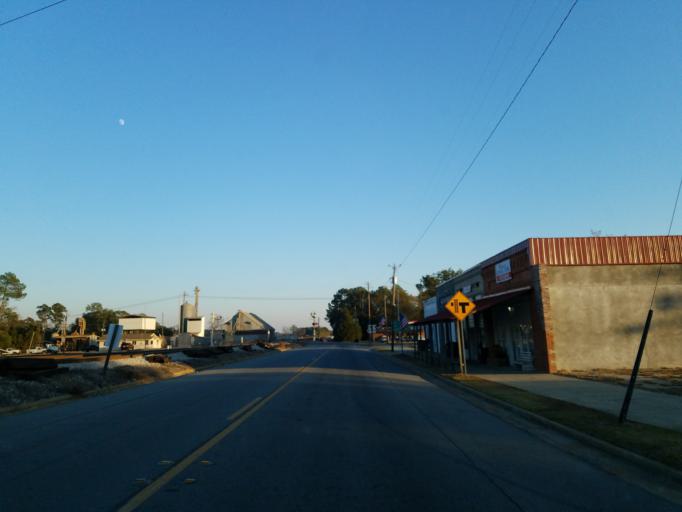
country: US
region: Georgia
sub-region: Wilcox County
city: Rochelle
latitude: 31.8073
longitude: -83.4877
